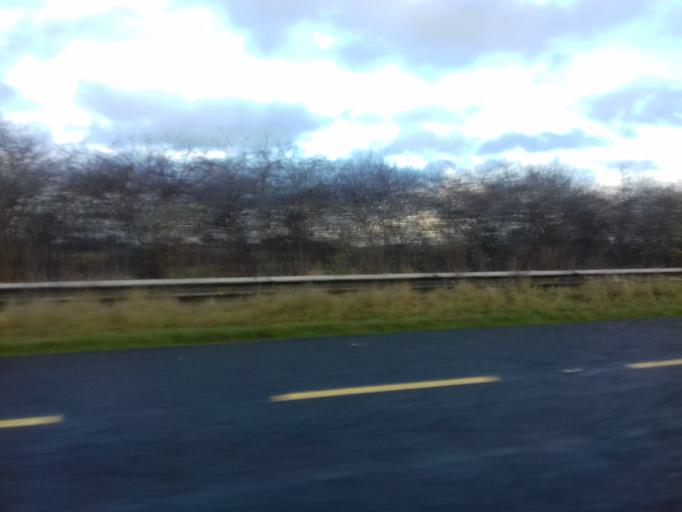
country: IE
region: Leinster
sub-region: Lu
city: Ardee
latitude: 53.8938
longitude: -6.5818
